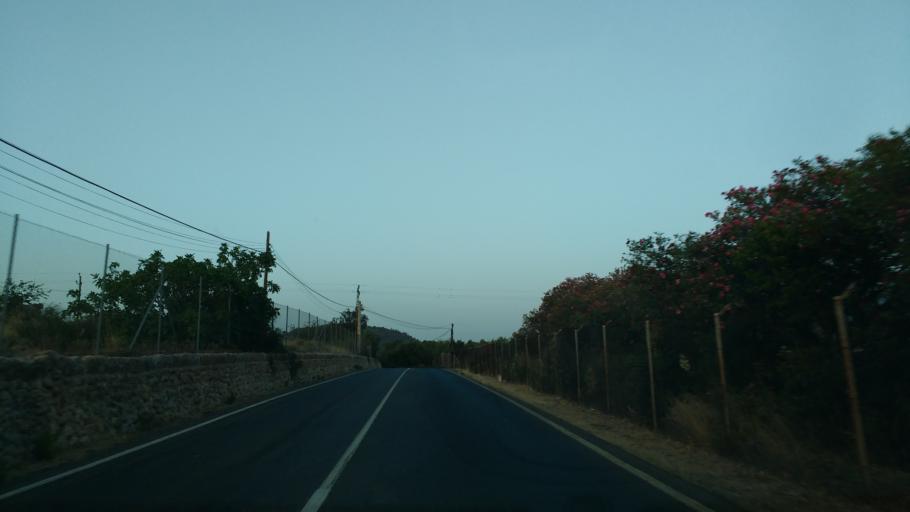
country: ES
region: Balearic Islands
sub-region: Illes Balears
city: Bunyola
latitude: 39.6658
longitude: 2.6909
